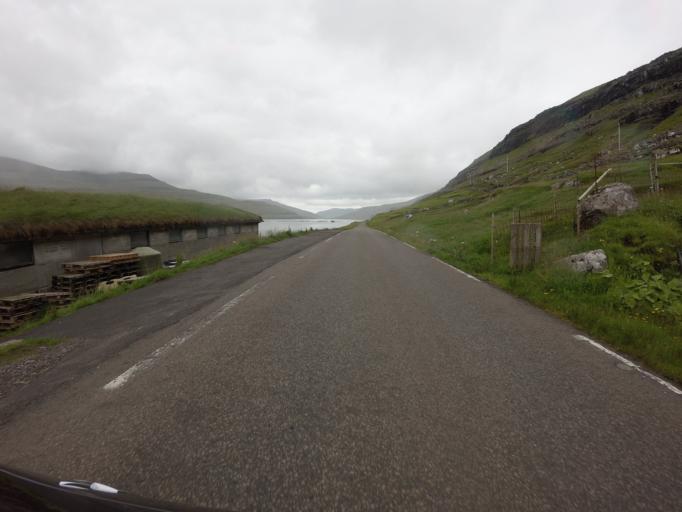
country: FO
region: Eysturoy
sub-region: Eidi
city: Eidi
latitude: 62.2681
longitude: -7.0846
